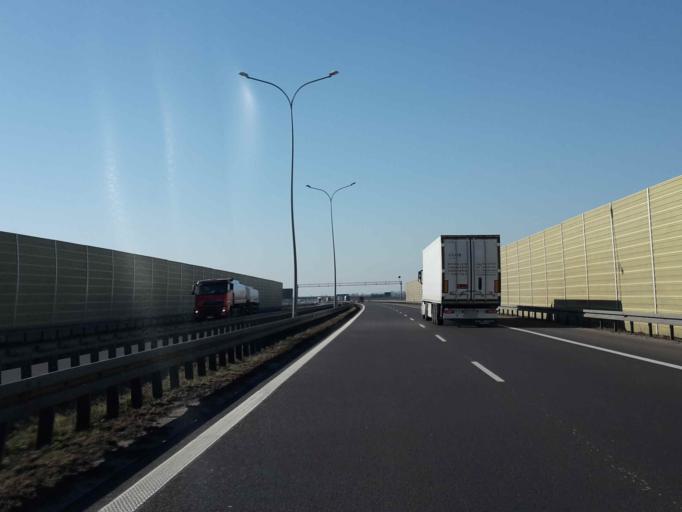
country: PL
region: Greater Poland Voivodeship
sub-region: Powiat poznanski
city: Kleszczewo
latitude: 52.3367
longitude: 17.1566
